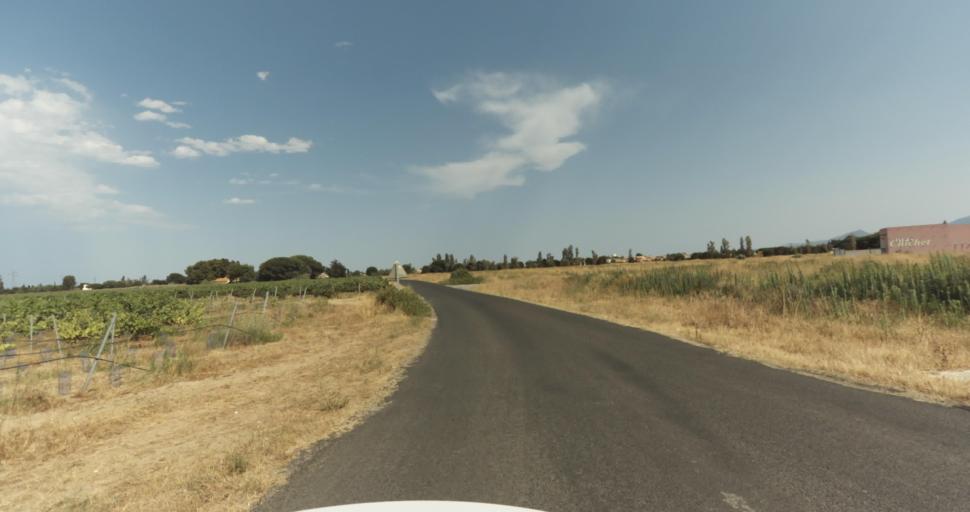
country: FR
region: Languedoc-Roussillon
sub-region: Departement des Pyrenees-Orientales
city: Alenya
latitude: 42.6457
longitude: 2.9683
